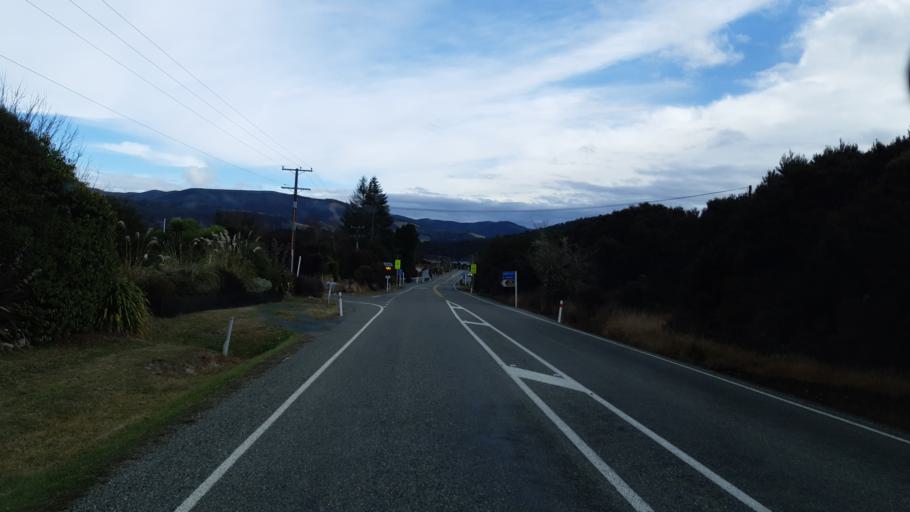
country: NZ
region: Tasman
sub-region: Tasman District
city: Wakefield
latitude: -41.8010
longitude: 172.8548
